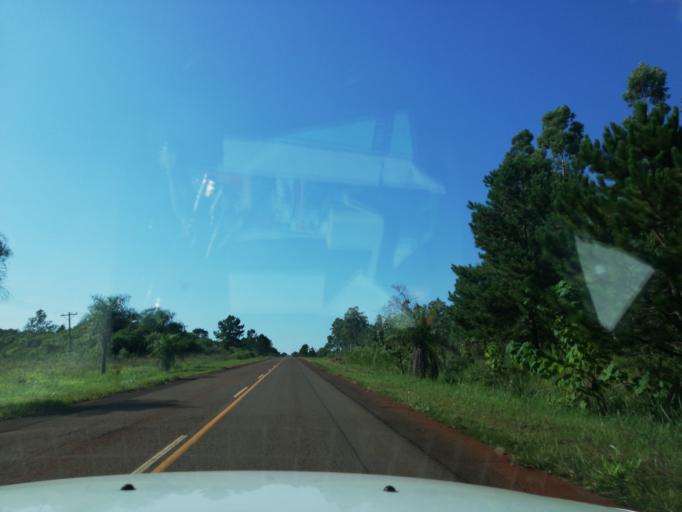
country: AR
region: Misiones
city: Bonpland
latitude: -27.4258
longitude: -55.5149
